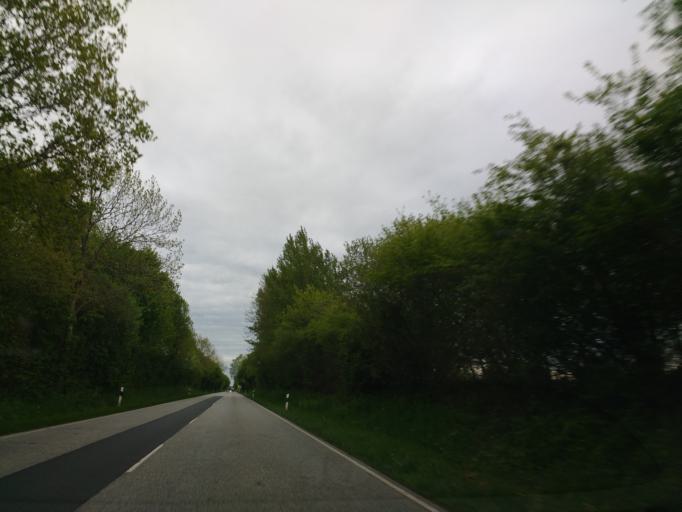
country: DE
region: Schleswig-Holstein
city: Dorphof
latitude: 54.6377
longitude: 9.9619
